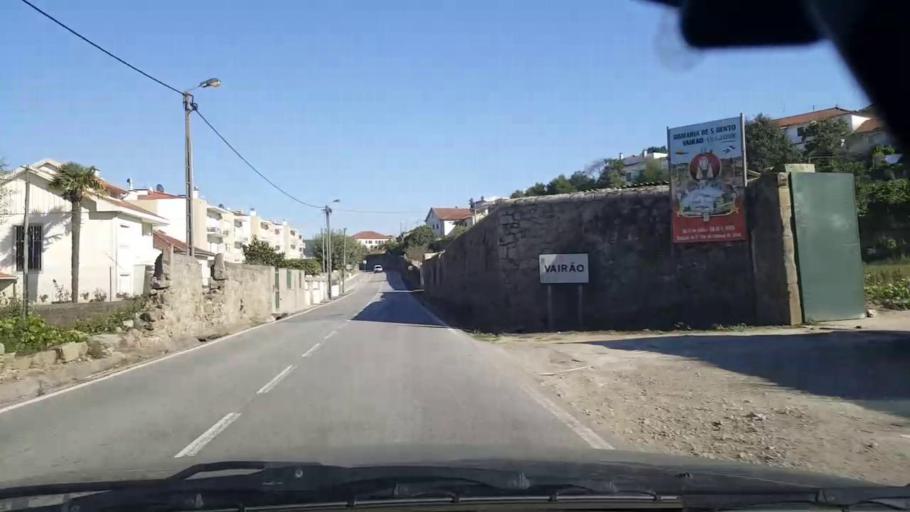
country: PT
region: Porto
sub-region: Vila do Conde
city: Arvore
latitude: 41.3343
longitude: -8.6696
